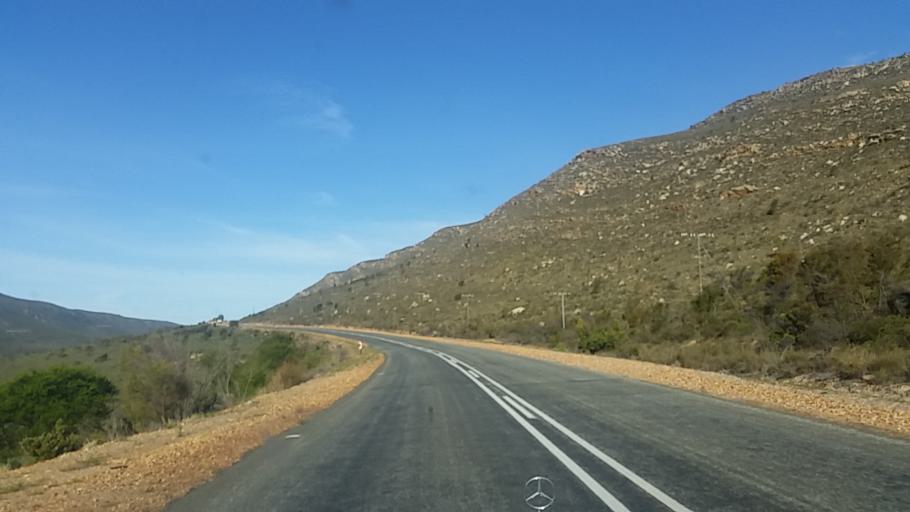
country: ZA
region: Western Cape
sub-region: Eden District Municipality
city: Knysna
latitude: -33.7501
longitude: 22.9656
